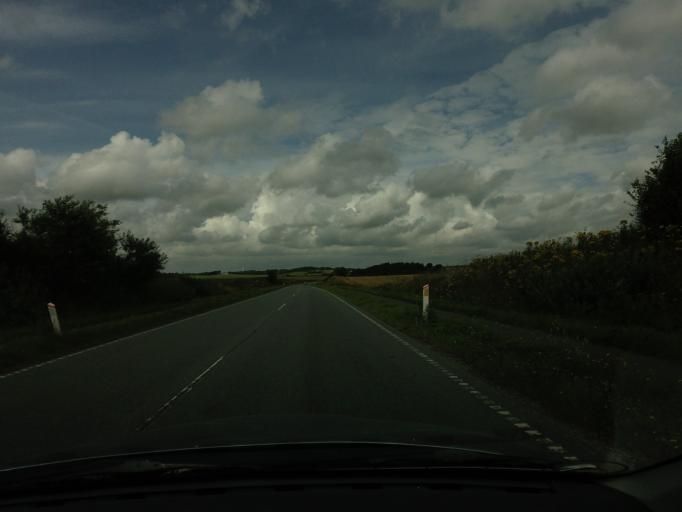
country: DK
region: North Denmark
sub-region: Hjorring Kommune
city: Tars
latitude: 57.3683
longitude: 10.1804
